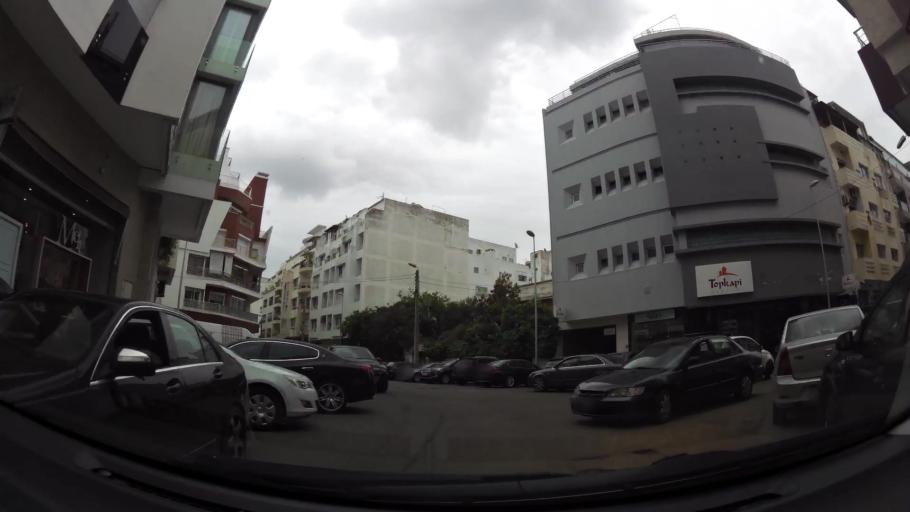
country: MA
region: Grand Casablanca
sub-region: Casablanca
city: Casablanca
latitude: 33.5924
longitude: -7.6444
